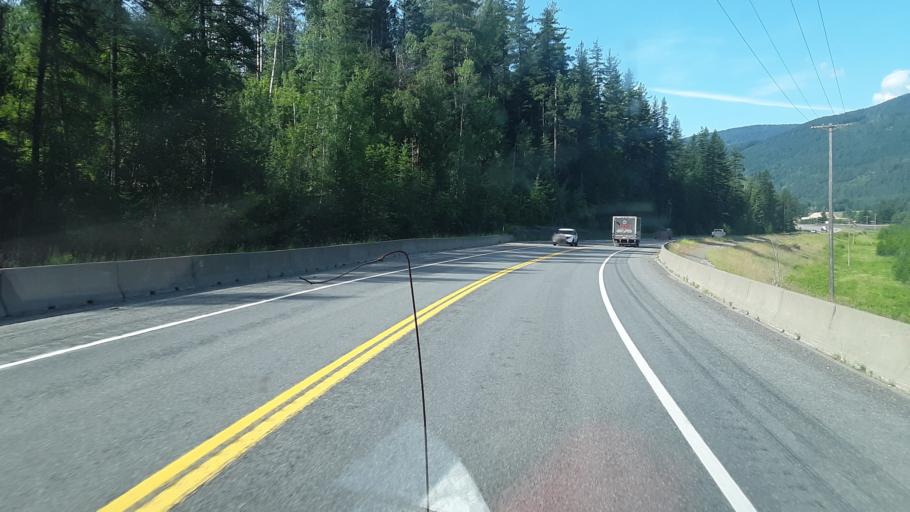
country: US
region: Idaho
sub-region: Bonner County
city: Ponderay
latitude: 48.4122
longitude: -116.5181
